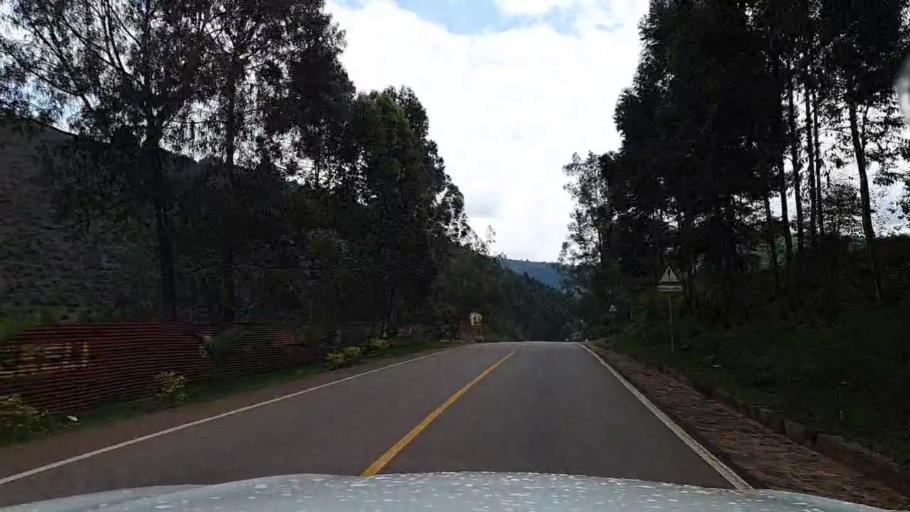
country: RW
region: Northern Province
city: Byumba
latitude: -1.7187
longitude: 30.1192
